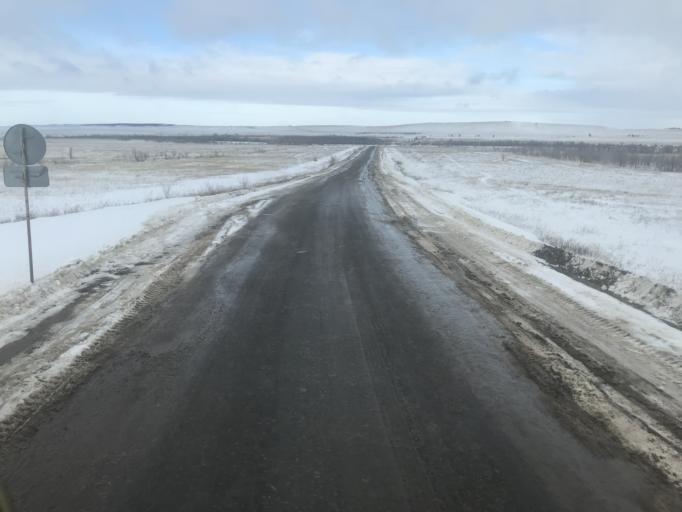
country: RU
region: Saratov
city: Staryye Ozinki
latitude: 51.2184
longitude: 49.8778
